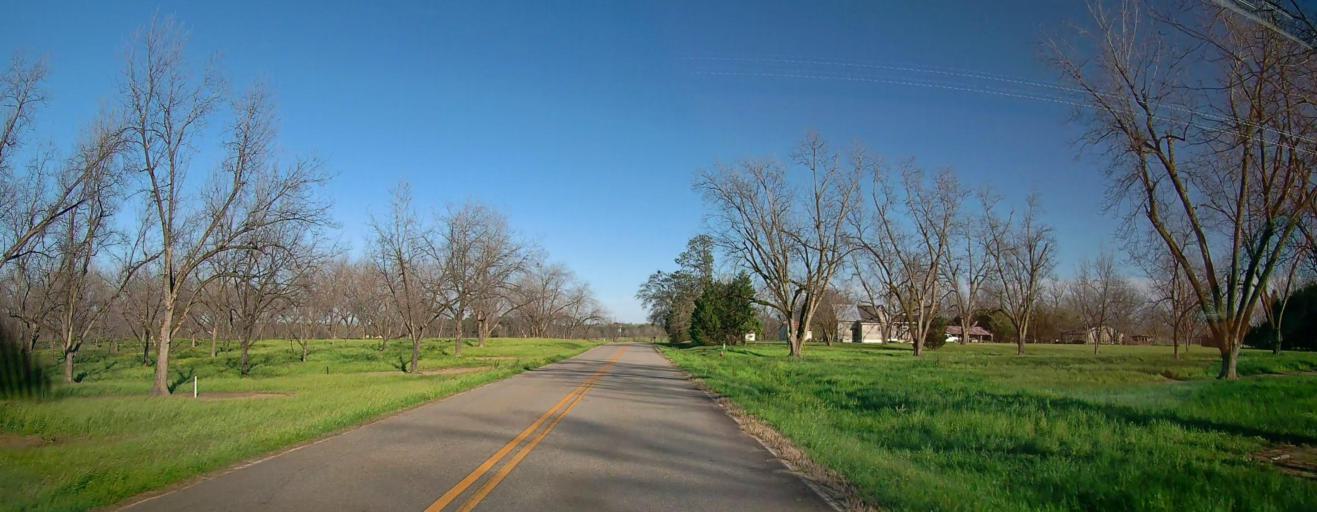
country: US
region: Georgia
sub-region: Houston County
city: Perry
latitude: 32.3677
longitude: -83.6858
